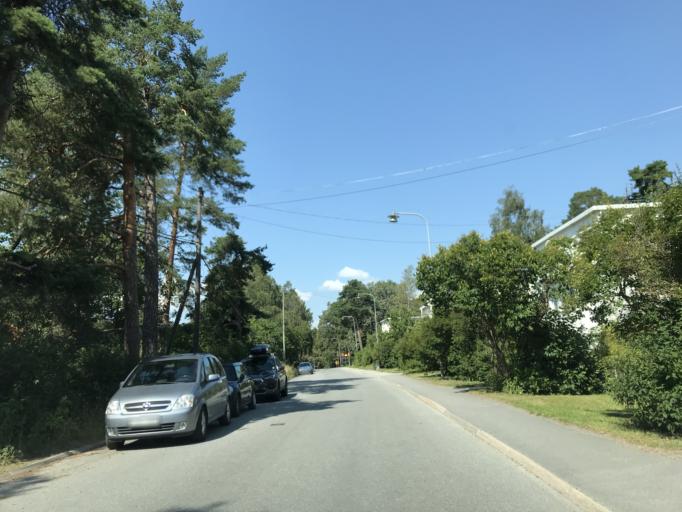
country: SE
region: Stockholm
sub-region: Stockholms Kommun
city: Bromma
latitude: 59.3336
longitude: 17.9564
